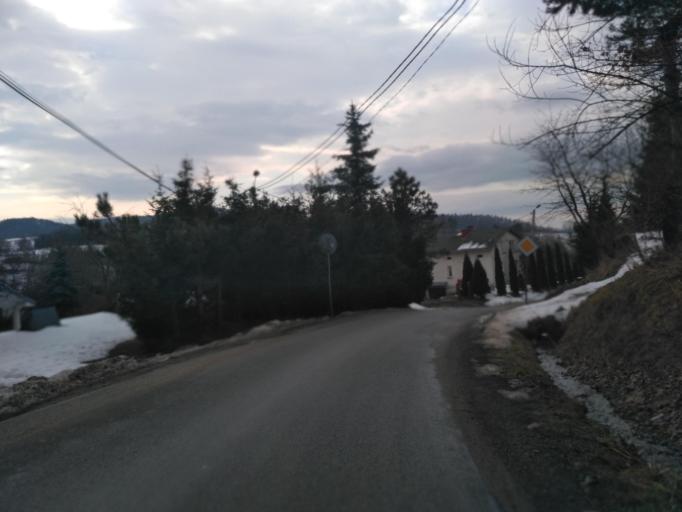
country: PL
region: Subcarpathian Voivodeship
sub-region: Powiat brzozowski
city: Dydnia
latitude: 49.6380
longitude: 22.1845
